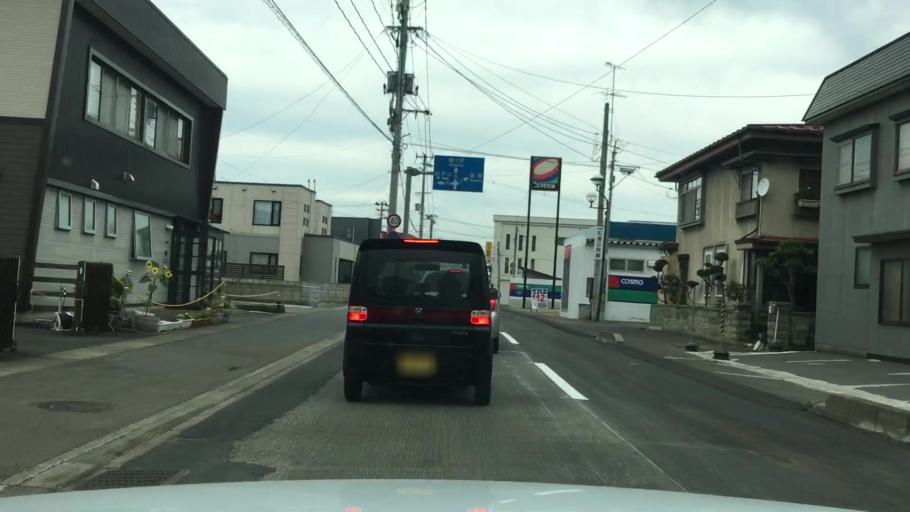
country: JP
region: Aomori
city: Hirosaki
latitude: 40.6279
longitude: 140.4542
